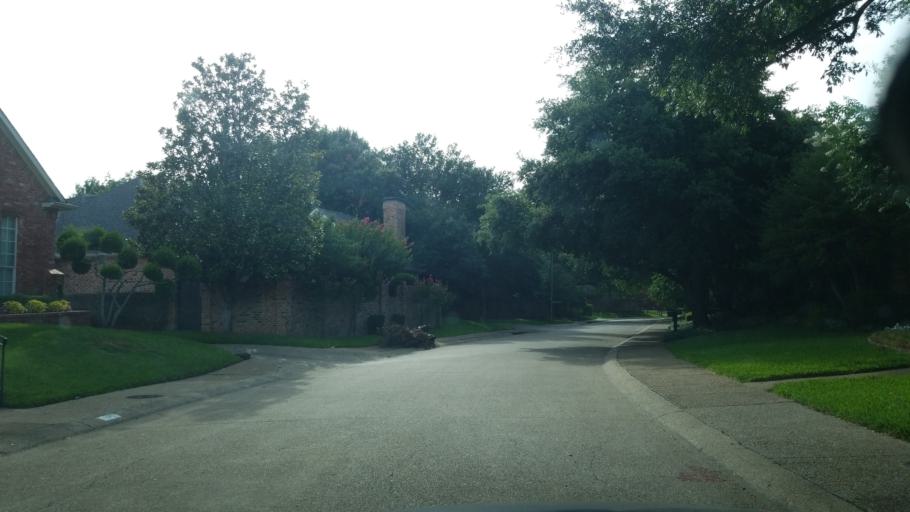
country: US
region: Texas
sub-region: Dallas County
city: University Park
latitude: 32.8704
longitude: -96.7810
